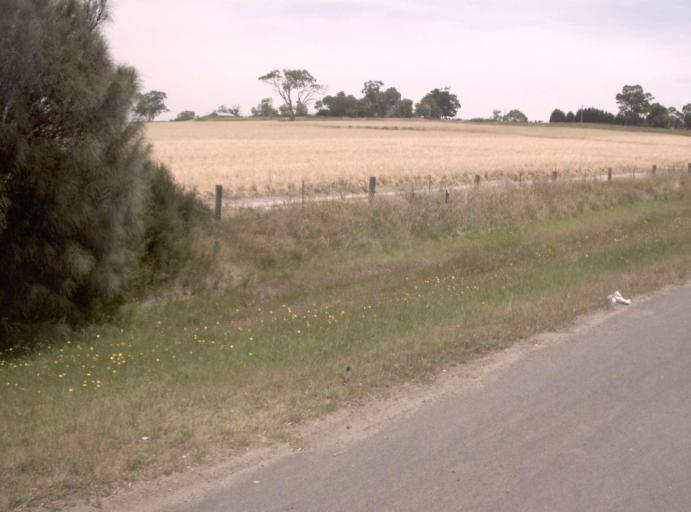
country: AU
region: Victoria
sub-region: Casey
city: Lynbrook
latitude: -38.0695
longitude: 145.2409
